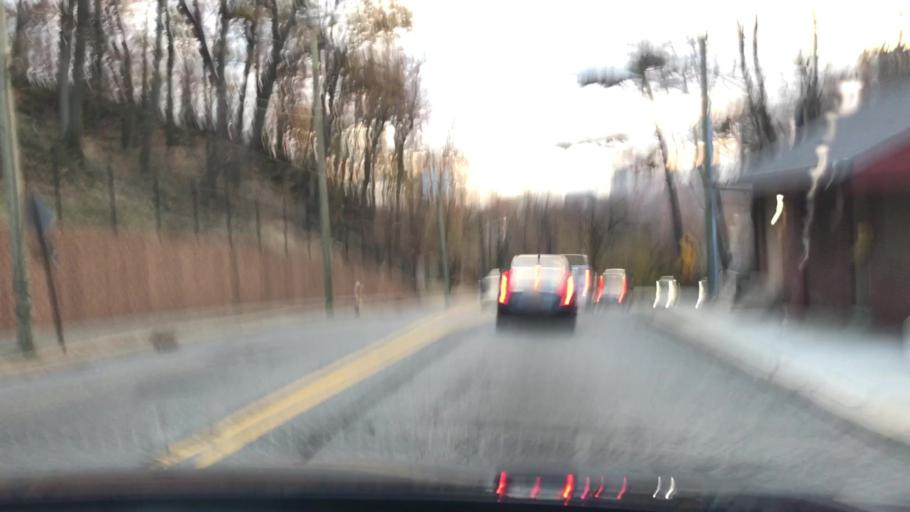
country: US
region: New Jersey
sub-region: Bergen County
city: Fort Lee
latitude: 40.8484
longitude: -73.9650
